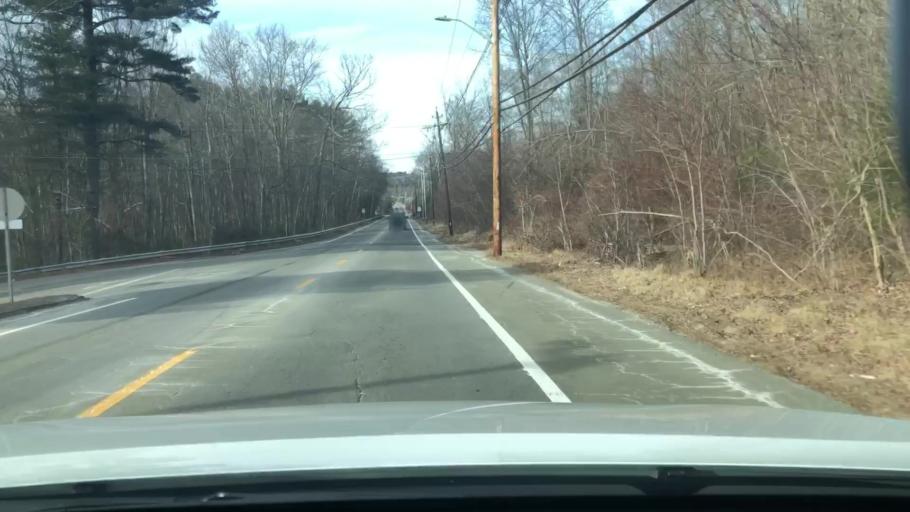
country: US
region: Massachusetts
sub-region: Worcester County
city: Hopedale
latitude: 42.1469
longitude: -71.5518
